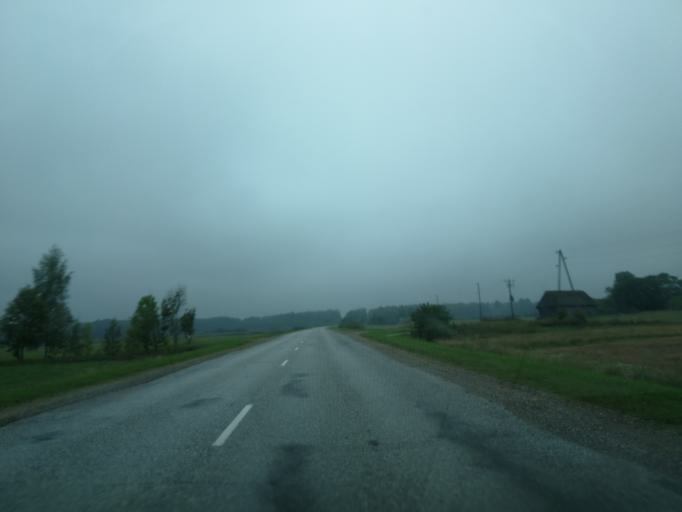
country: LV
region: Varkava
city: Vecvarkava
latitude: 56.3145
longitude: 26.5056
